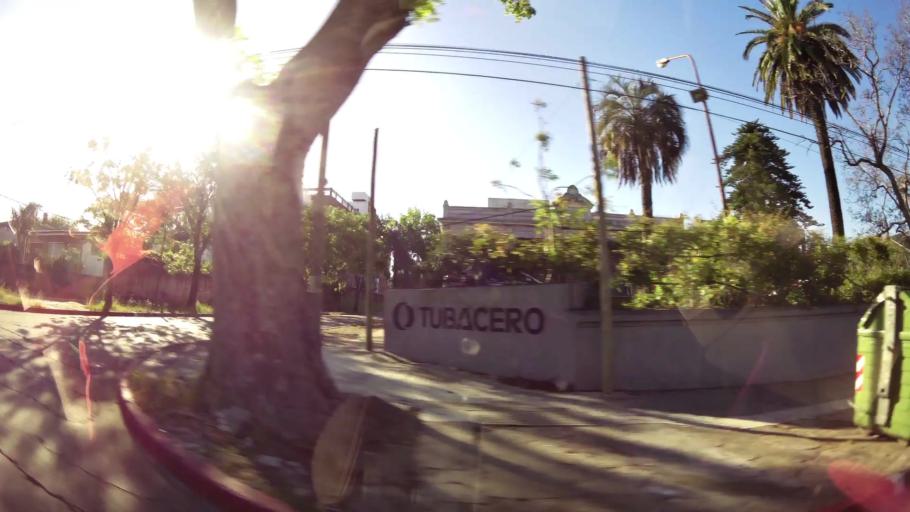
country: UY
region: Montevideo
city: Montevideo
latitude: -34.8440
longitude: -56.2022
